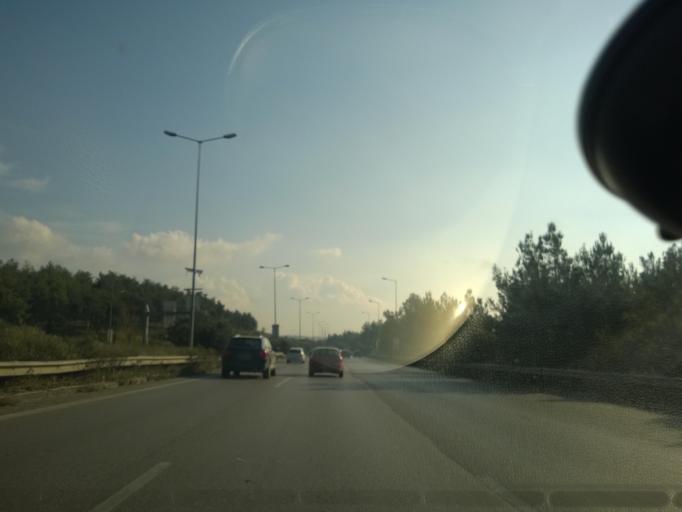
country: GR
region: Central Macedonia
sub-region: Nomos Thessalonikis
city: Triandria
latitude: 40.6211
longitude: 22.9824
